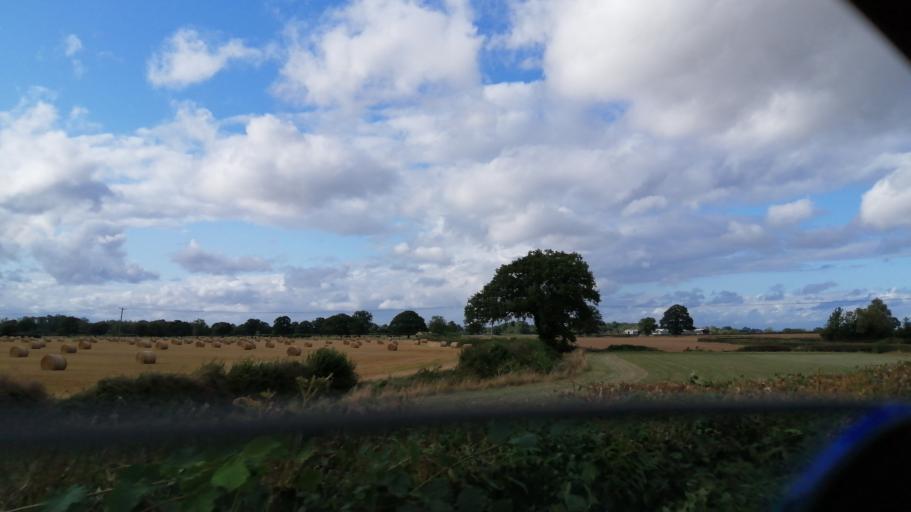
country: GB
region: England
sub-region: Herefordshire
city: Thruxton
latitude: 51.9974
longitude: -2.7732
